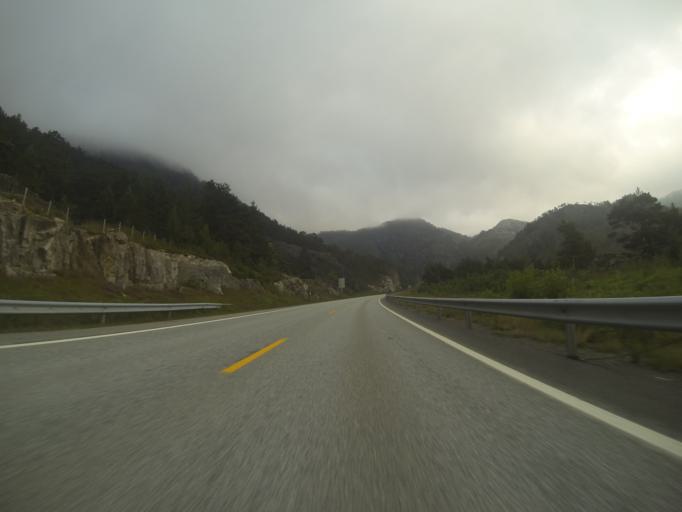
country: NO
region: Hordaland
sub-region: Odda
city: Odda
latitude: 59.8806
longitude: 6.4319
